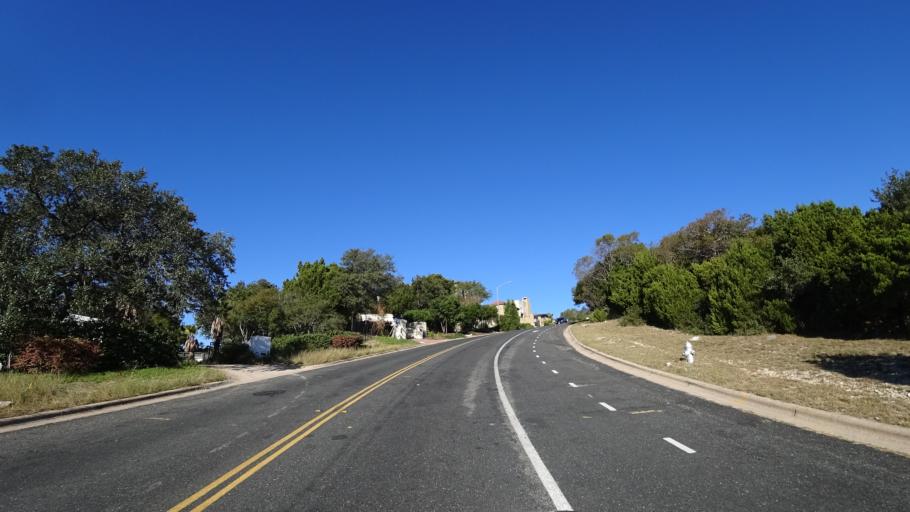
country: US
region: Texas
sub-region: Travis County
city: West Lake Hills
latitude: 30.3576
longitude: -97.8000
